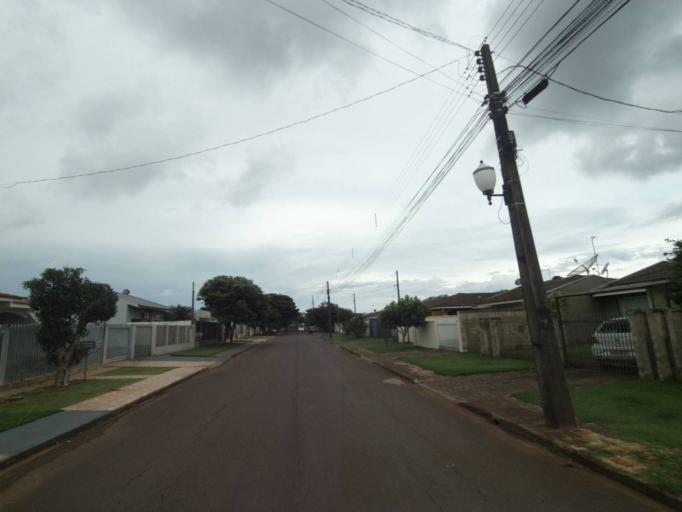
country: BR
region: Parana
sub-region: Campo Mourao
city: Campo Mourao
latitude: -24.0219
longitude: -52.3577
